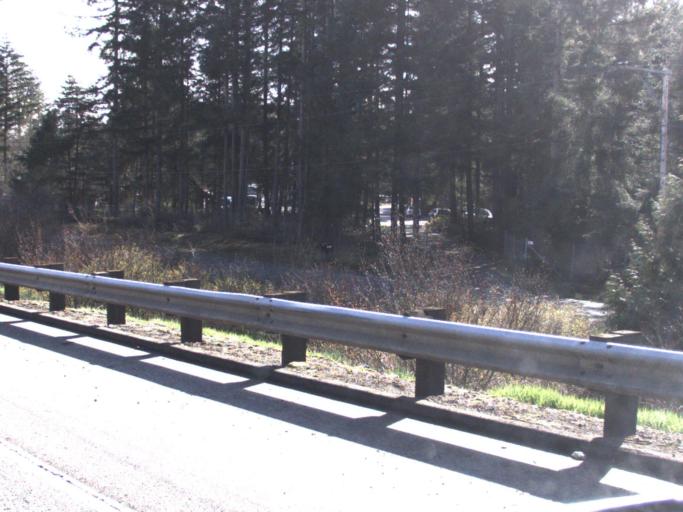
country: US
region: Washington
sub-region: King County
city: Covington
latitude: 47.3486
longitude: -122.1373
